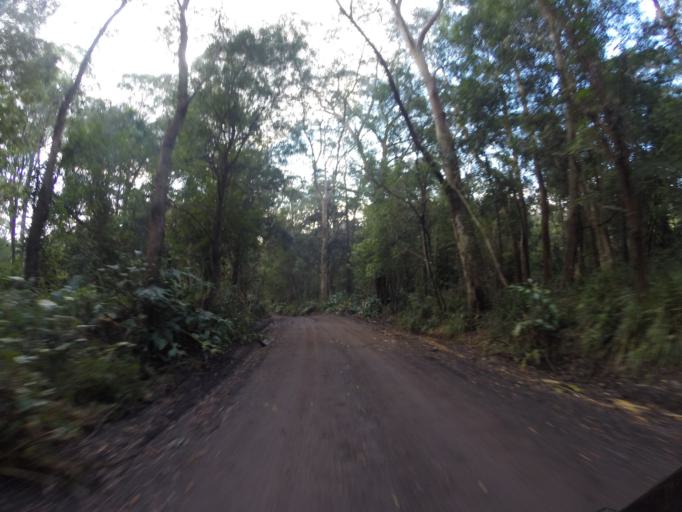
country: AU
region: New South Wales
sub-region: Wollongong
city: Cordeaux Heights
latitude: -34.4295
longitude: 150.7828
